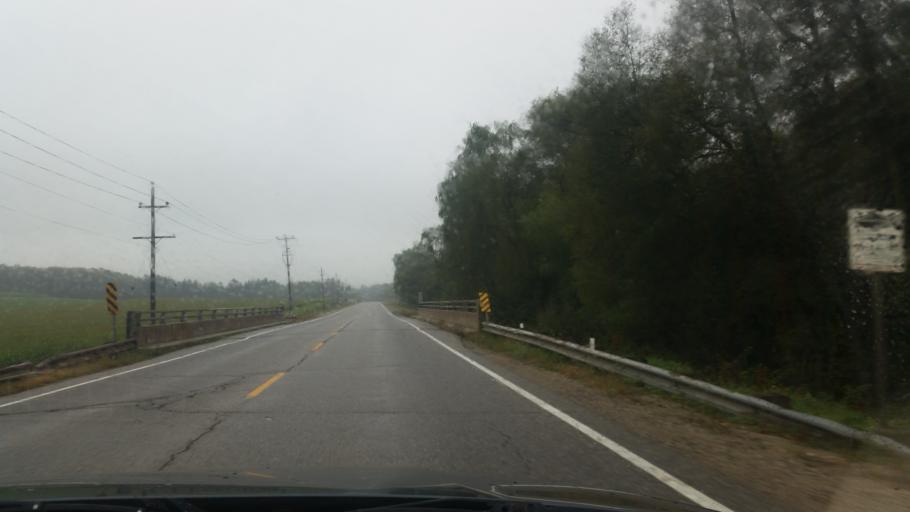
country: CA
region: Ontario
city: Waterloo
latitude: 43.6551
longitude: -80.4971
